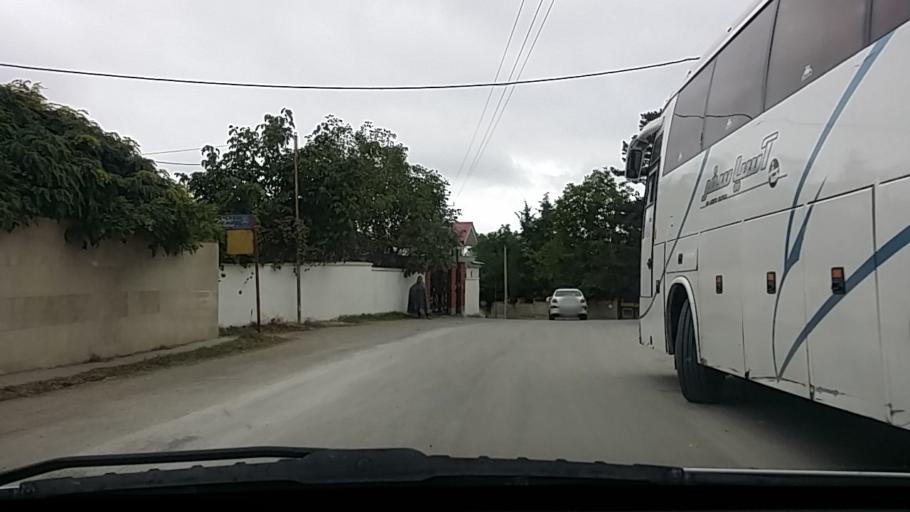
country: IR
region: Mazandaran
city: `Abbasabad
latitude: 36.5017
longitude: 51.1590
